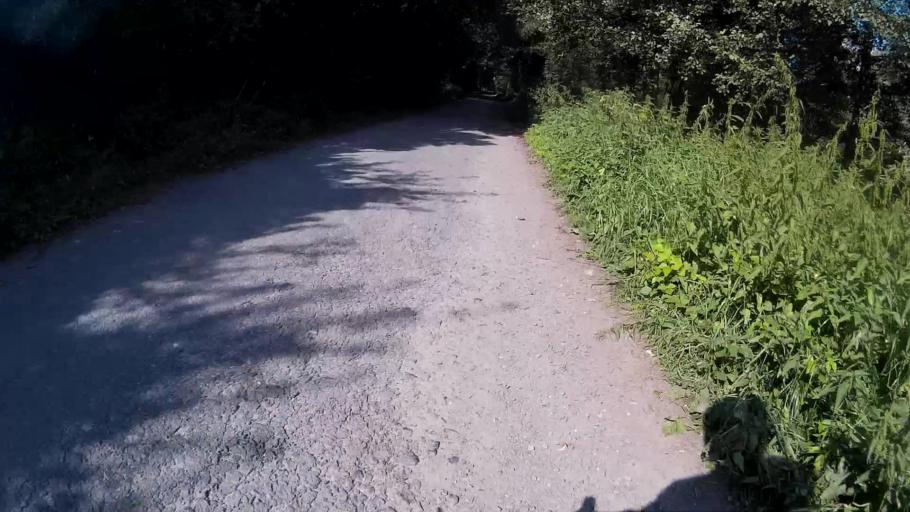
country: CZ
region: South Moravian
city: Hrusovany nad Jevisovkou
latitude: 48.7927
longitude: 16.4316
